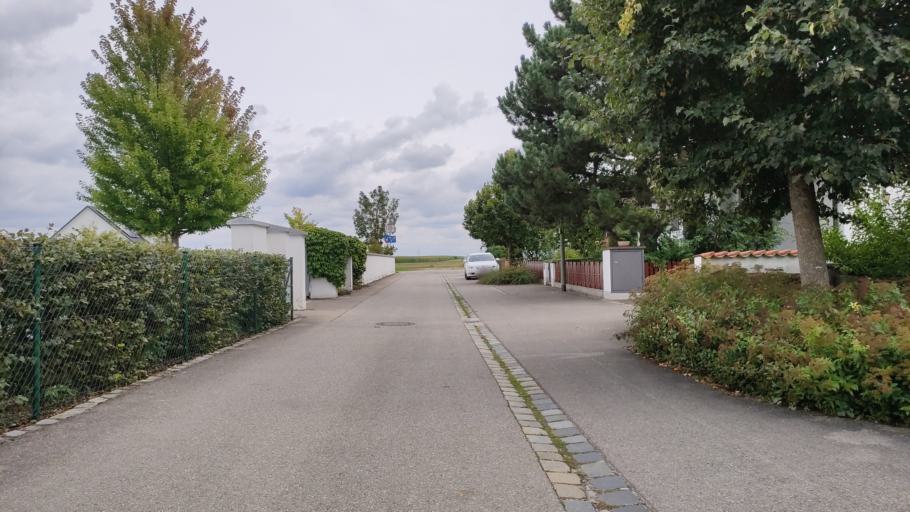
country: DE
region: Bavaria
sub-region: Swabia
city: Wehringen
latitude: 48.2450
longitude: 10.8038
